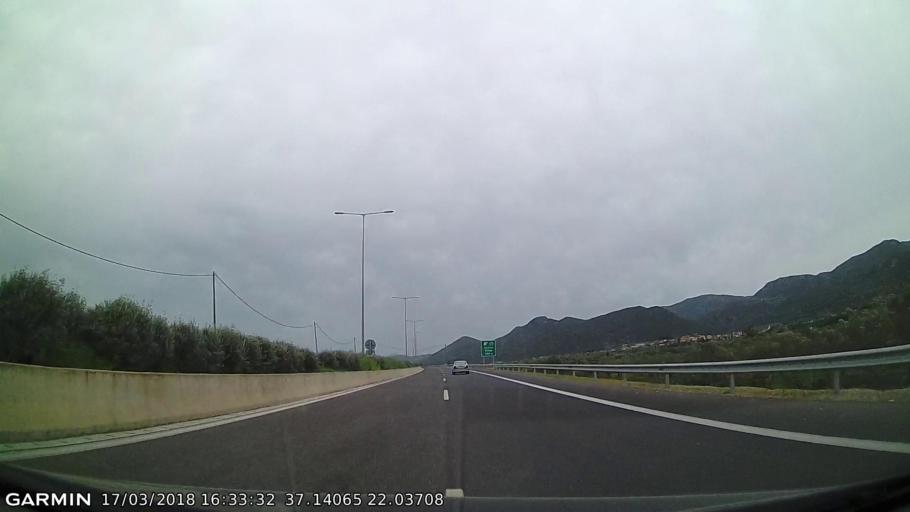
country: GR
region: Peloponnese
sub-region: Nomos Messinias
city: Arfara
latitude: 37.1423
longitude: 22.0364
